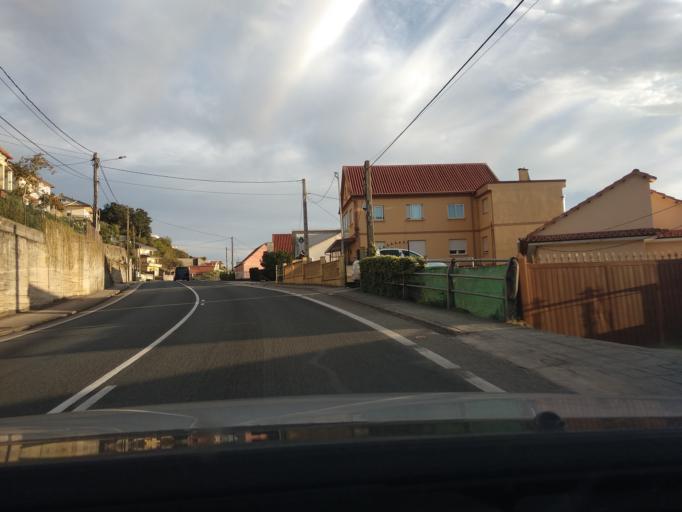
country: ES
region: Galicia
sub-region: Provincia de Pontevedra
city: Moana
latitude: 42.2876
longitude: -8.7163
